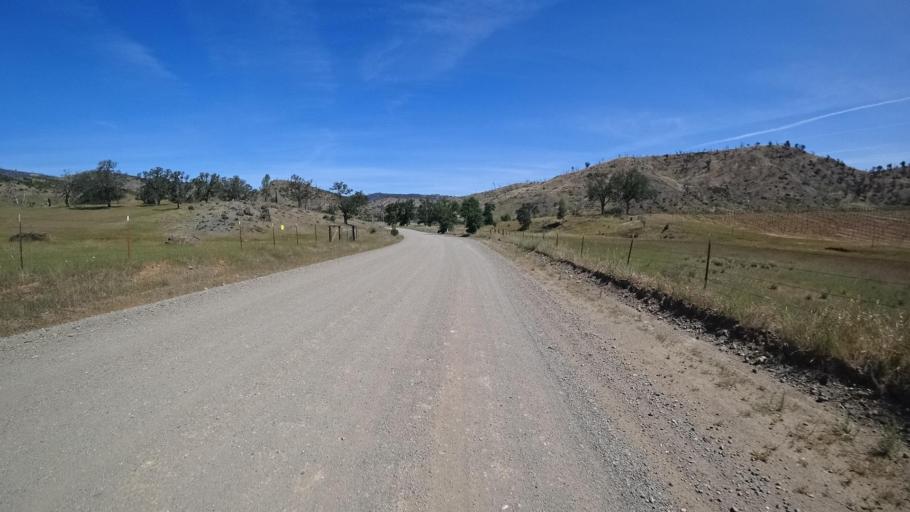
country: US
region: California
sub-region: Lake County
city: Middletown
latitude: 38.7918
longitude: -122.6129
